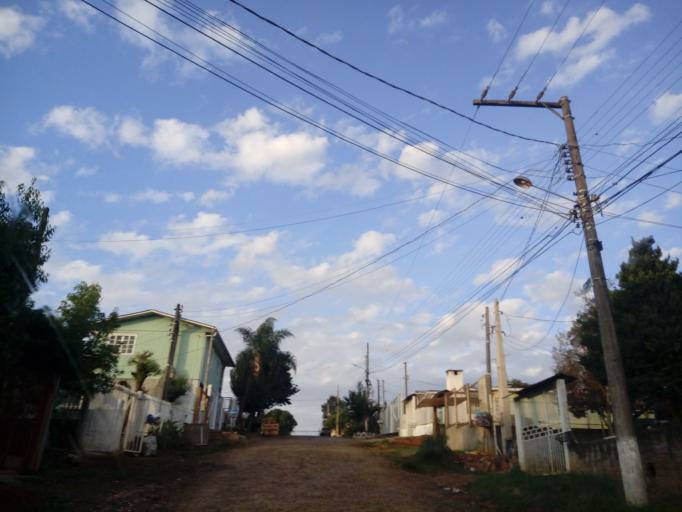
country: BR
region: Santa Catarina
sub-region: Chapeco
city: Chapeco
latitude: -27.1200
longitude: -52.6253
